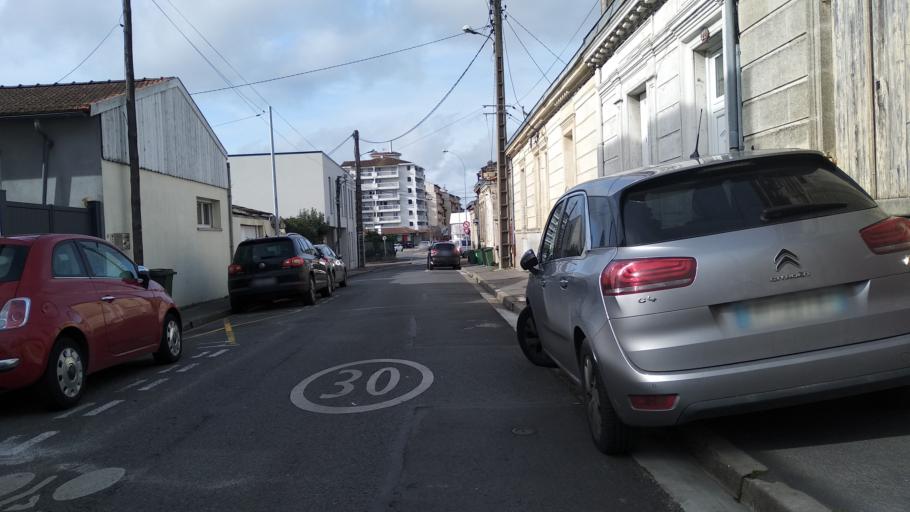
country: FR
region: Aquitaine
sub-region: Departement de la Gironde
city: Talence
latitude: 44.8182
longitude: -0.5988
